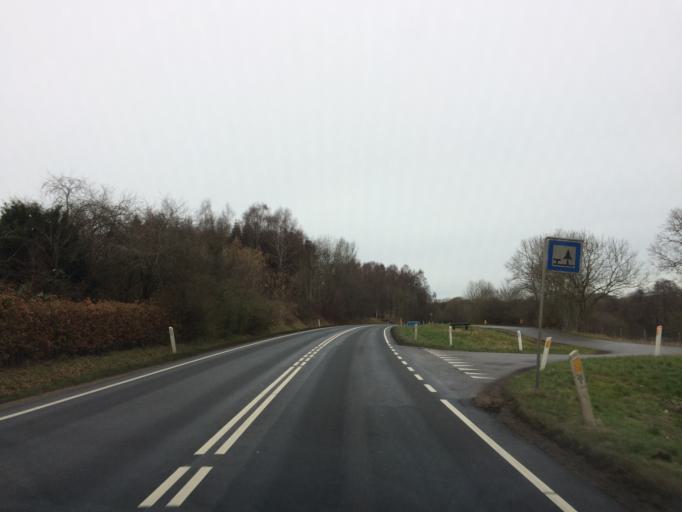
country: DK
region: Zealand
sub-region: Holbaek Kommune
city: Jyderup
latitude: 55.6299
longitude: 11.3918
